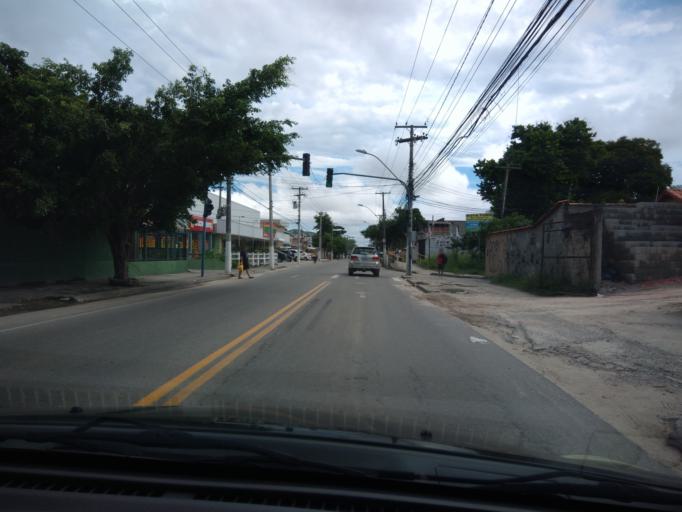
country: BR
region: Rio de Janeiro
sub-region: Niteroi
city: Niteroi
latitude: -22.9402
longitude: -43.0278
